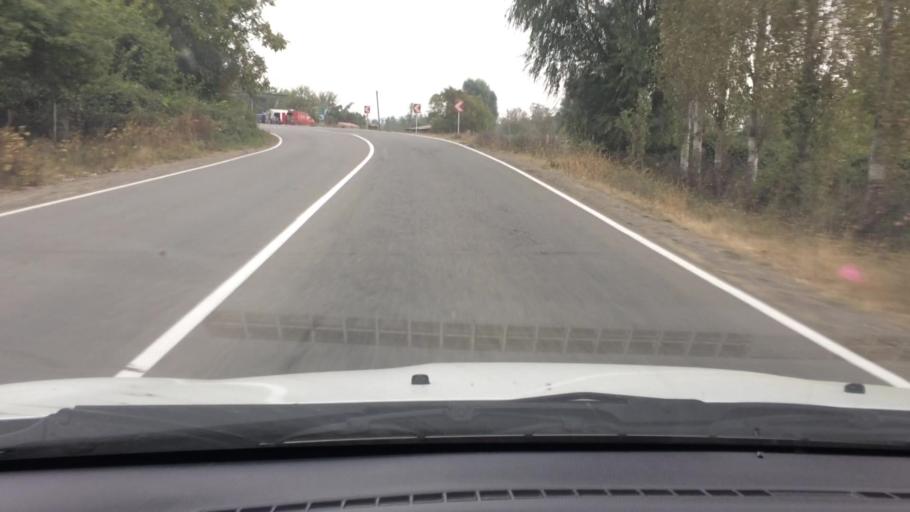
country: GE
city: Naghvarevi
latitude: 41.3056
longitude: 44.7909
